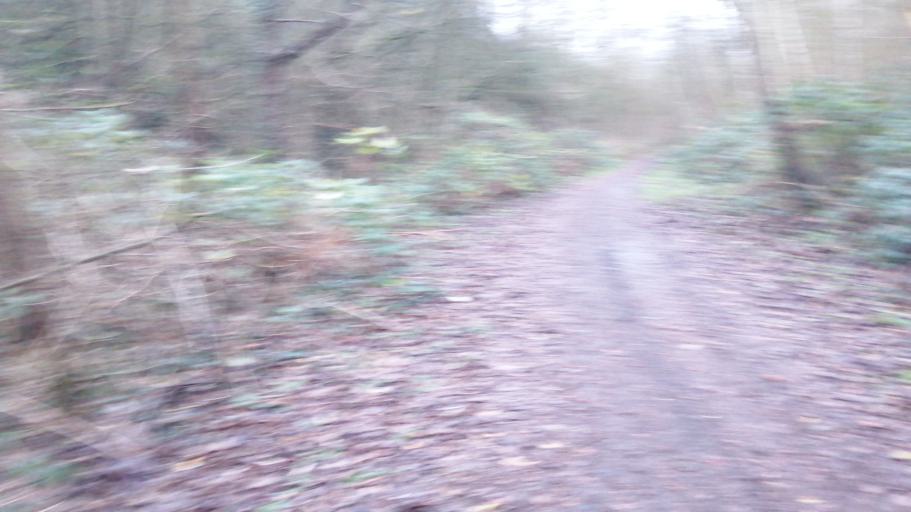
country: FR
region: Nord-Pas-de-Calais
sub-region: Departement du Pas-de-Calais
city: Billy-Montigny
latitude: 50.4071
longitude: 2.9171
